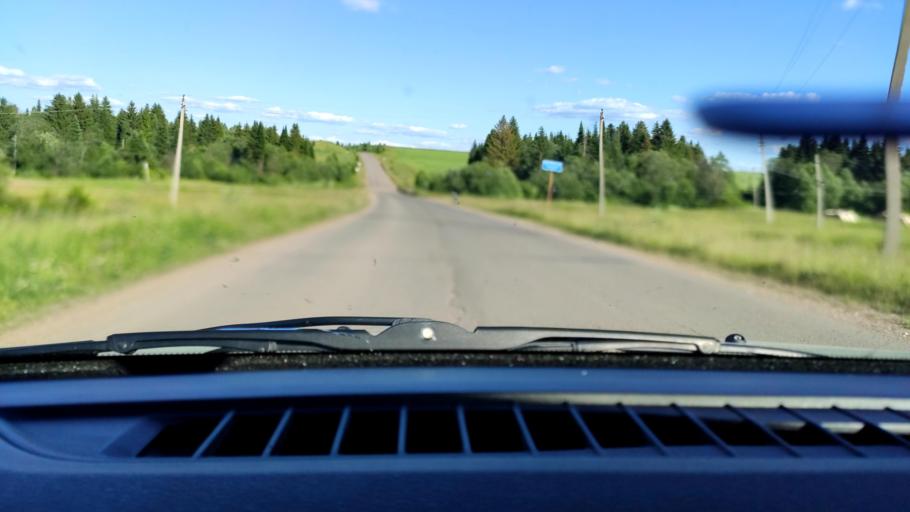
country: RU
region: Perm
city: Uinskoye
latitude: 57.0737
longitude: 56.5609
